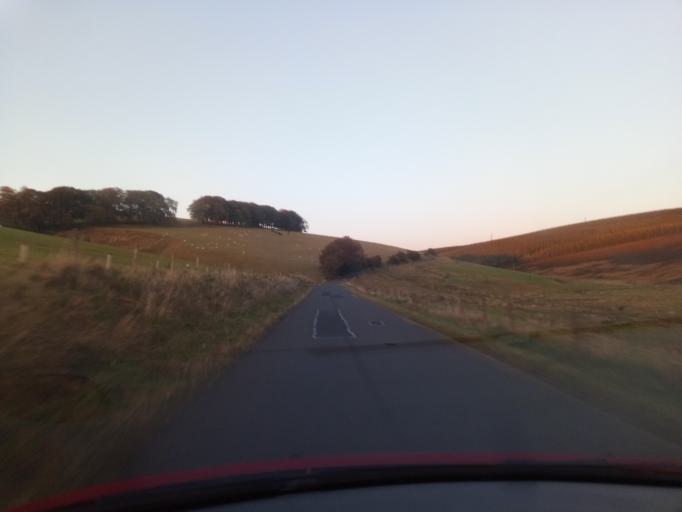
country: GB
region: Scotland
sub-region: Fife
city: Pathhead
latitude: 55.7847
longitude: -2.9034
